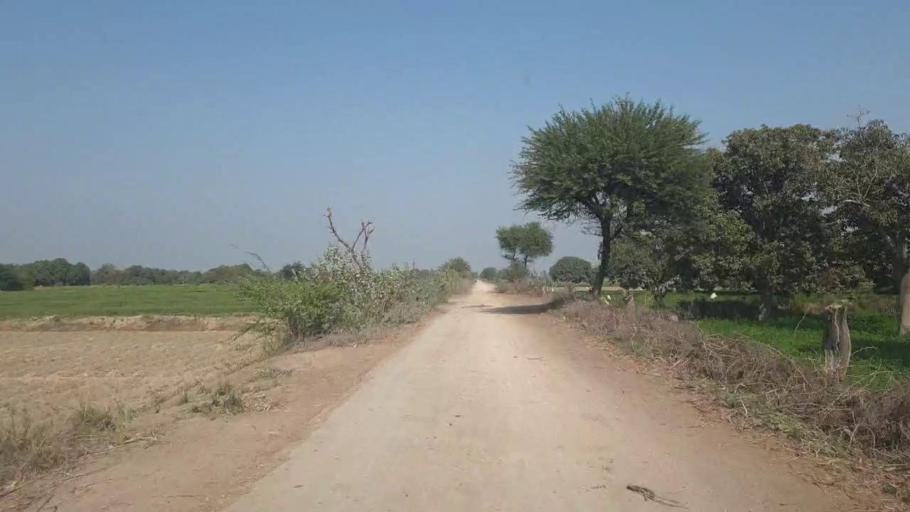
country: PK
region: Sindh
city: Tando Allahyar
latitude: 25.4404
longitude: 68.8499
